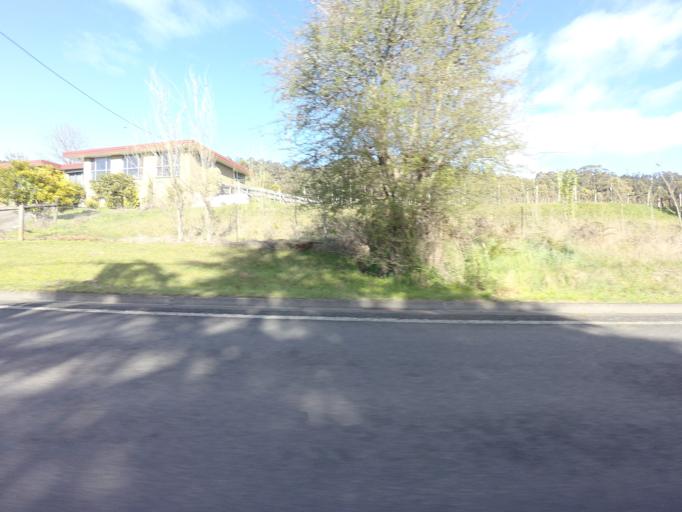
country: AU
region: Tasmania
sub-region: Huon Valley
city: Cygnet
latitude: -43.3077
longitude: 147.0109
